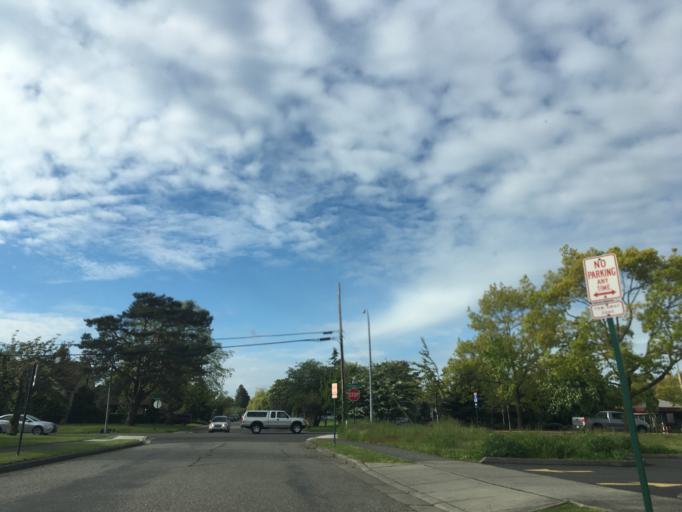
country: US
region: Washington
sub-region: Whatcom County
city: Bellingham
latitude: 48.7625
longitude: -122.4664
